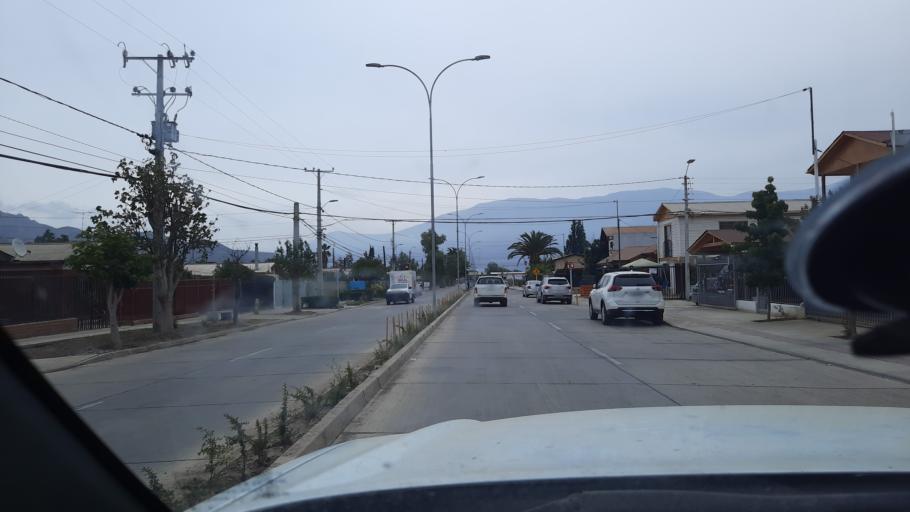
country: CL
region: Valparaiso
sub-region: Provincia de San Felipe
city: San Felipe
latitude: -32.7436
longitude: -70.7176
